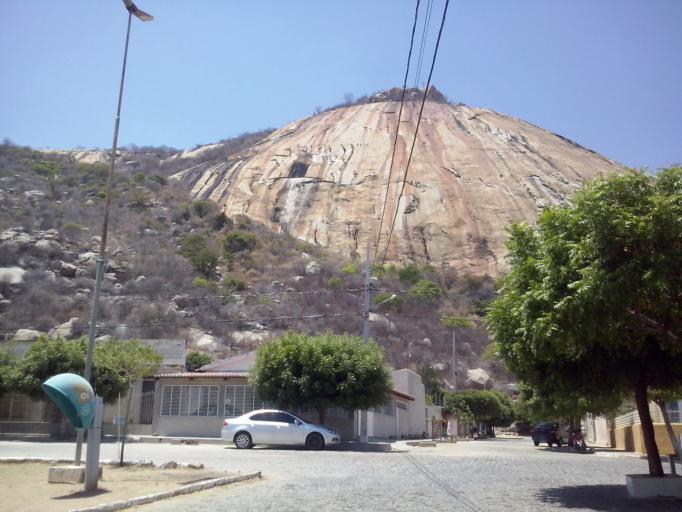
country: BR
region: Rio Grande do Norte
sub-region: Jardim De Piranhas
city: Jardim de Piranhas
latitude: -6.3510
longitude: -37.4946
